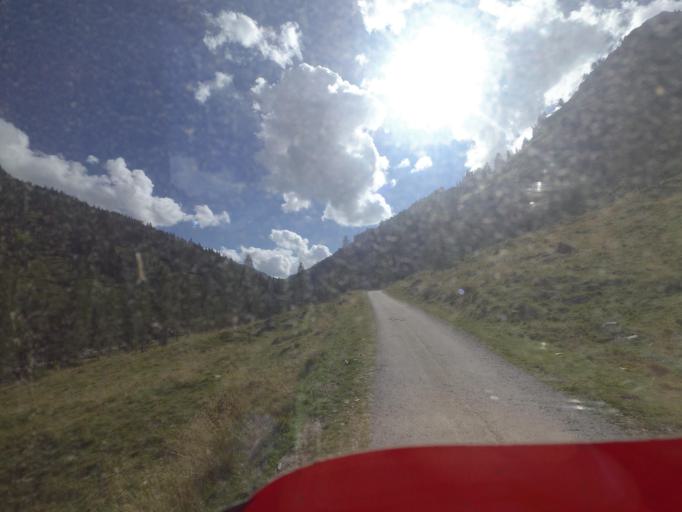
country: AT
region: Salzburg
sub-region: Politischer Bezirk Sankt Johann im Pongau
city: Kleinarl
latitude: 47.1849
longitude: 13.3601
